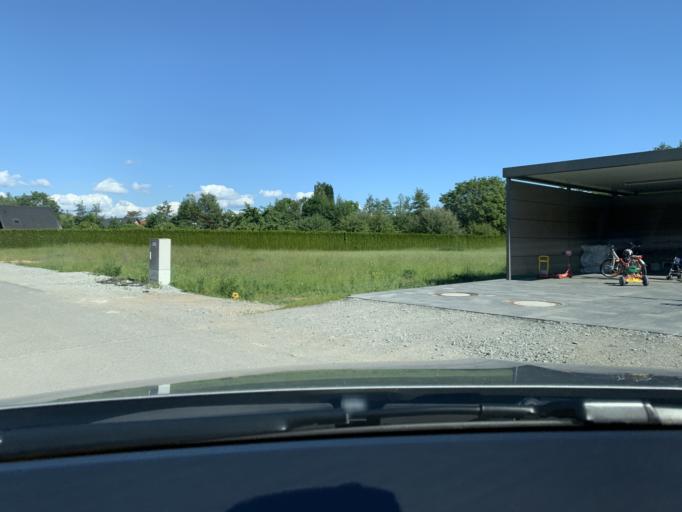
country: DE
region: North Rhine-Westphalia
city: Rietberg
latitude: 51.8129
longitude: 8.4195
